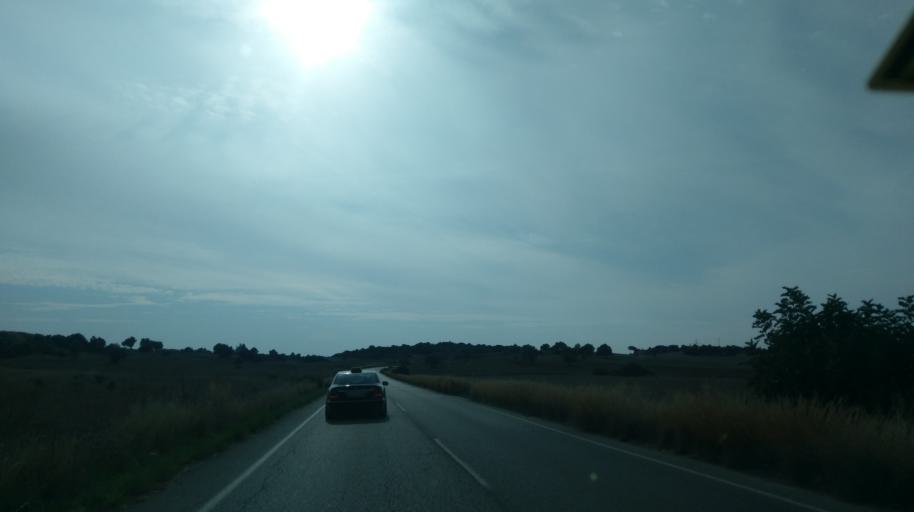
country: CY
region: Ammochostos
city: Leonarisso
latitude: 35.3932
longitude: 34.0605
